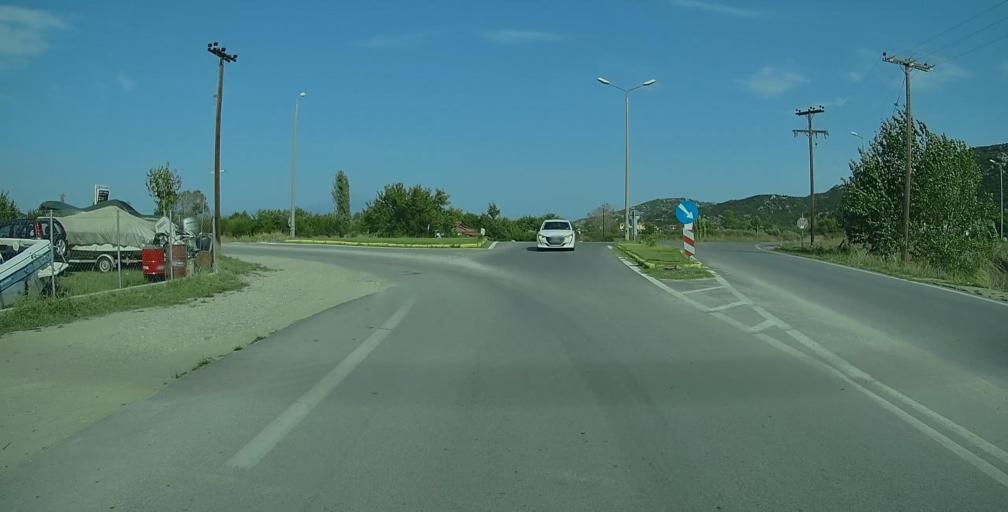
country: GR
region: Central Macedonia
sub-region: Nomos Chalkidikis
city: Sykia
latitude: 40.0336
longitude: 23.9682
